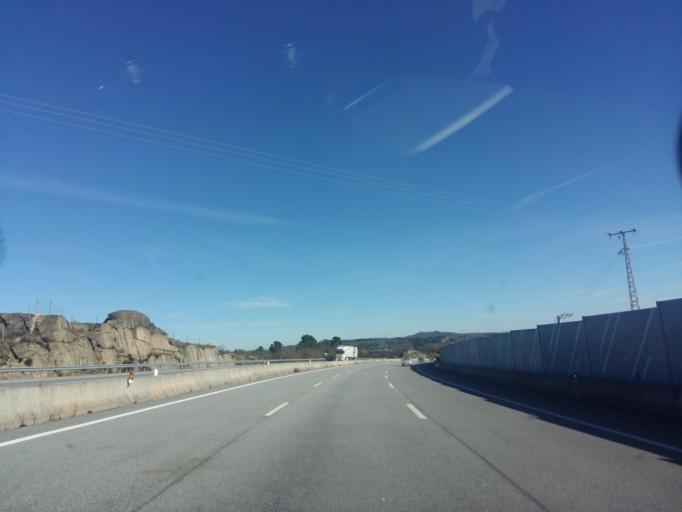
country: PT
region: Guarda
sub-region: Guarda
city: Sequeira
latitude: 40.5723
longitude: -7.2095
